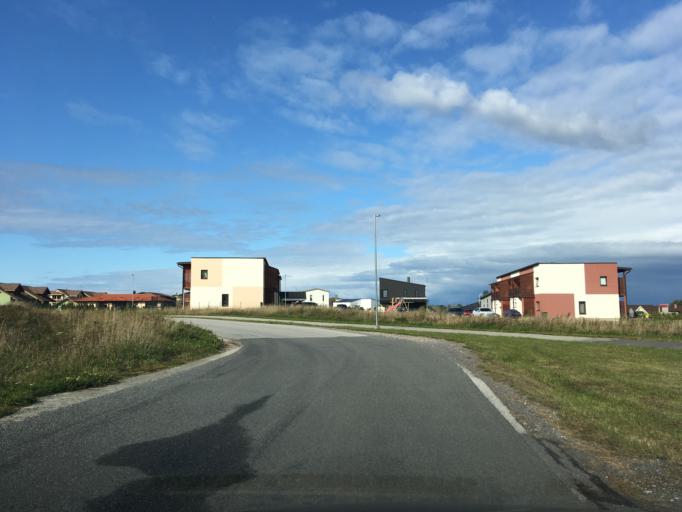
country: EE
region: Harju
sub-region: Saue vald
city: Laagri
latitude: 59.3451
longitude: 24.6465
